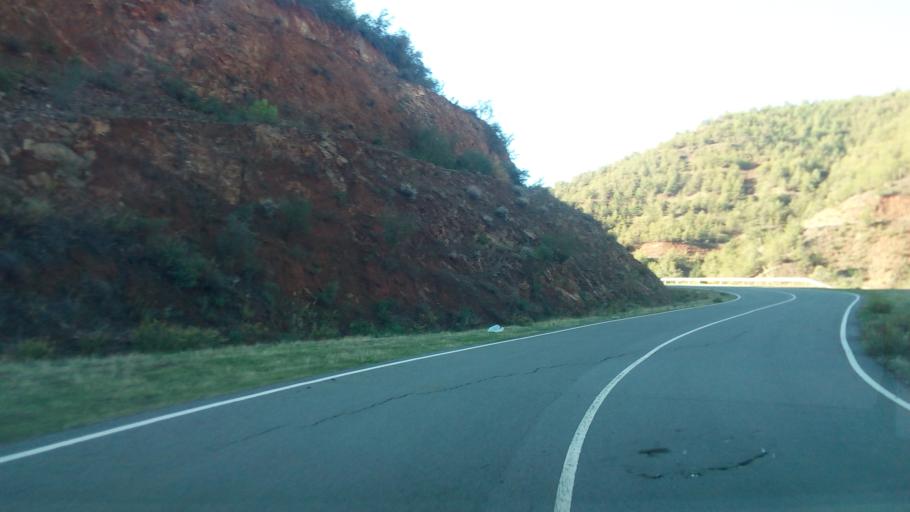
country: CY
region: Lefkosia
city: Lefka
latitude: 35.0960
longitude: 32.7623
